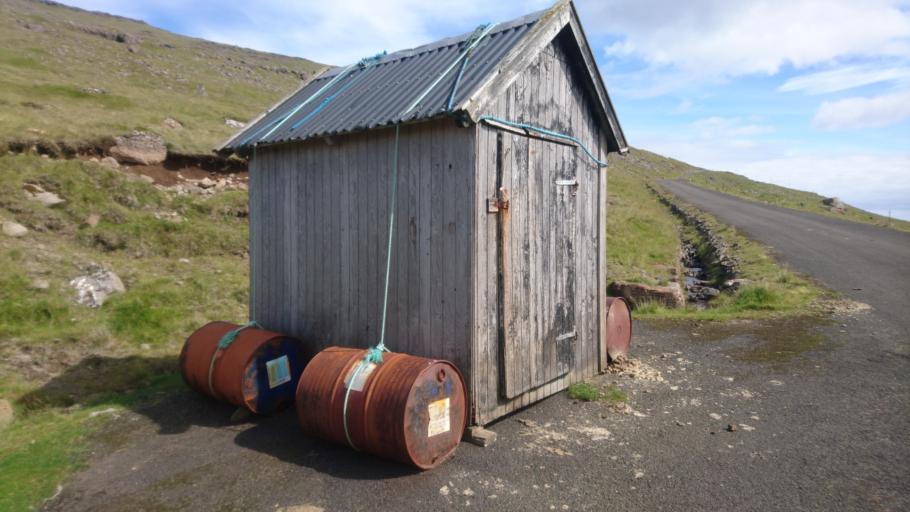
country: FO
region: Nordoyar
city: Klaksvik
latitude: 62.3210
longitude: -6.3036
